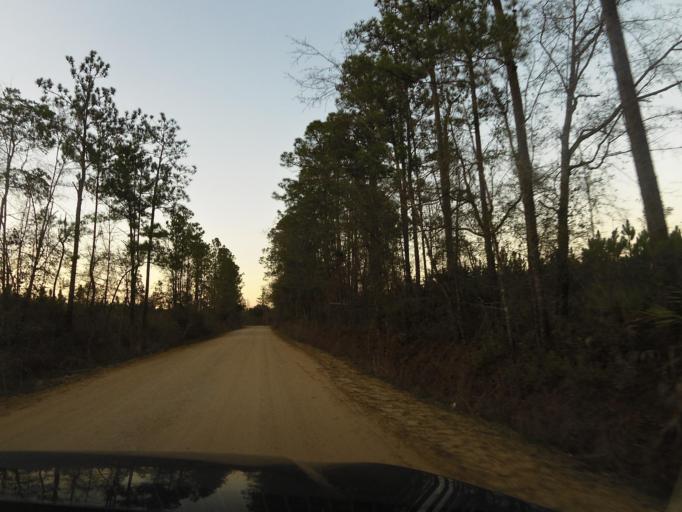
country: US
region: Florida
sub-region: Clay County
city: Asbury Lake
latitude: 29.9537
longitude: -81.7890
